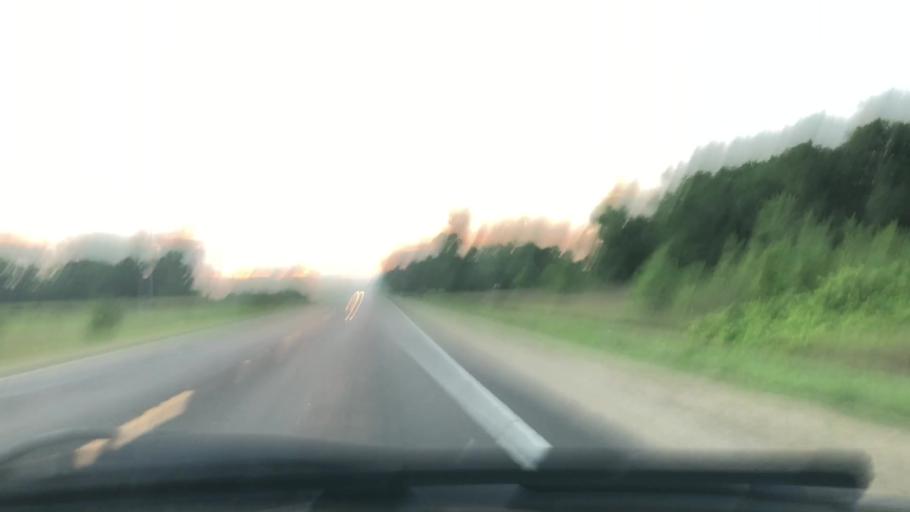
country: US
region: Wisconsin
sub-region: Sauk County
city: Spring Green
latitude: 43.1992
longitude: -90.2403
